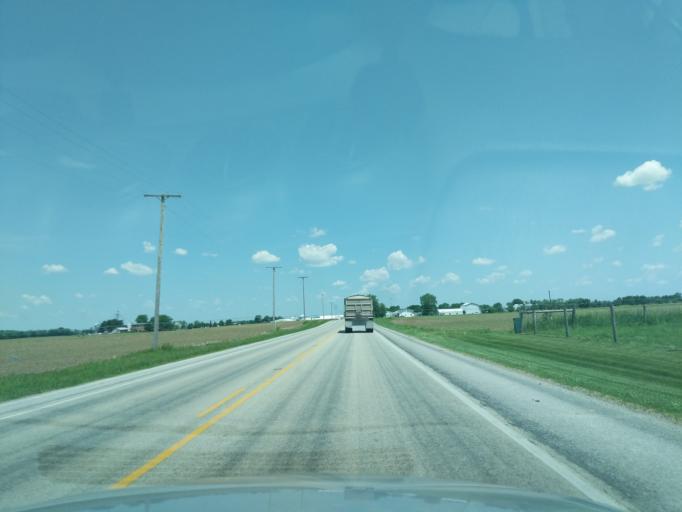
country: US
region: Indiana
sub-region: LaGrange County
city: Topeka
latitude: 41.5147
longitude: -85.5779
